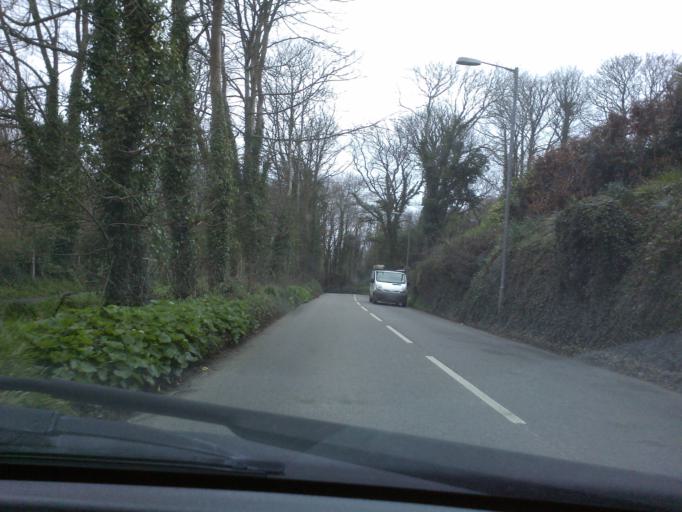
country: GB
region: England
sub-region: Cornwall
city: Penzance
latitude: 50.1089
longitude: -5.5564
